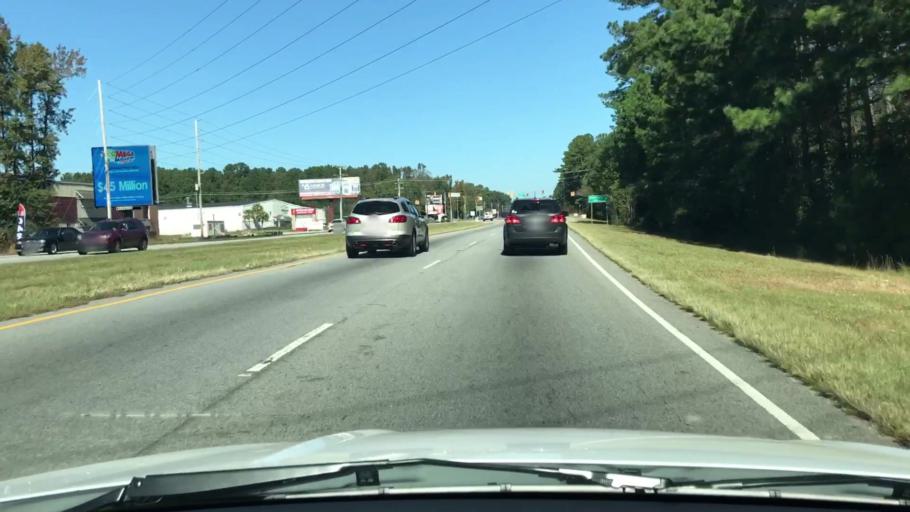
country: US
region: South Carolina
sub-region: Beaufort County
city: Bluffton
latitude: 32.3215
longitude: -80.9337
